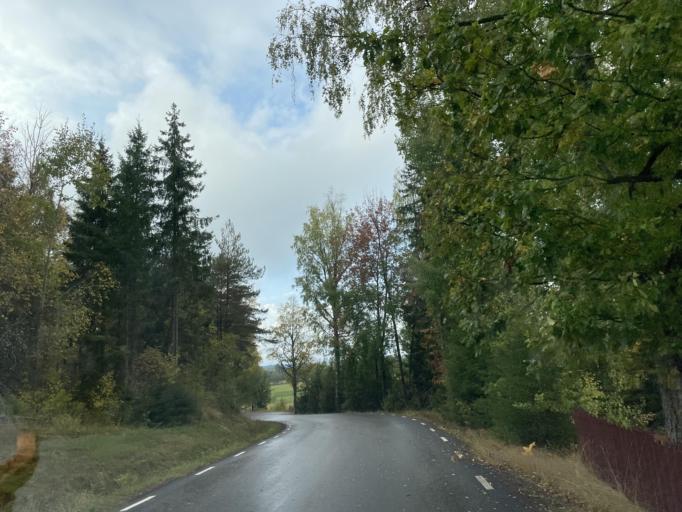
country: SE
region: Vaermland
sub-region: Karlstads Kommun
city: Skattkarr
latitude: 59.4511
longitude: 13.6086
